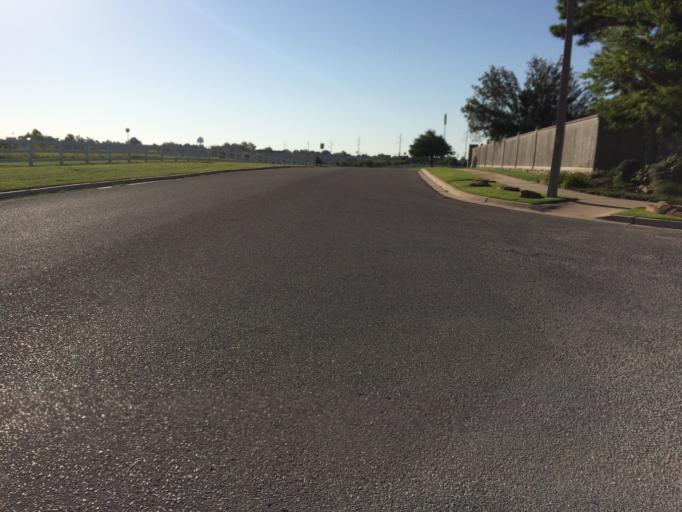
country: US
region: Oklahoma
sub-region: Cleveland County
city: Norman
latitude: 35.2128
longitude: -97.4908
